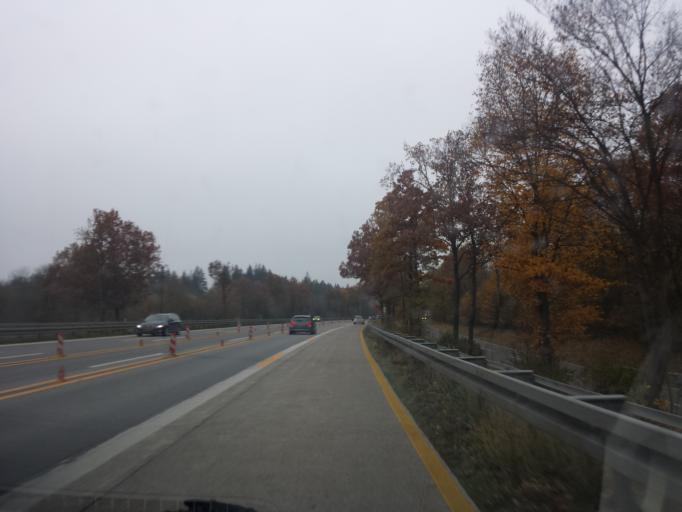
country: DE
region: Bavaria
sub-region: Upper Bavaria
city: Neuried
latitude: 48.0607
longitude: 11.4717
